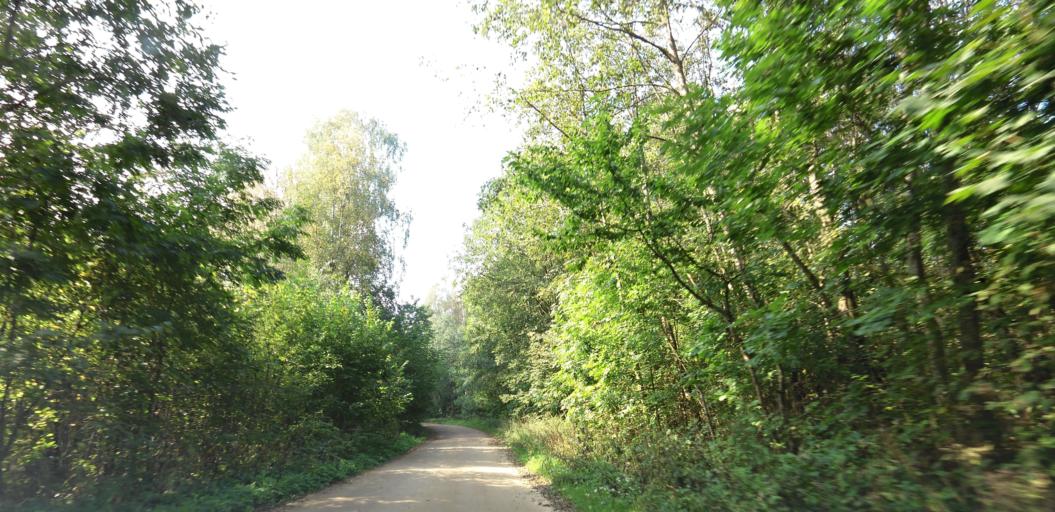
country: LT
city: Grigiskes
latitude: 54.7730
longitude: 25.0601
